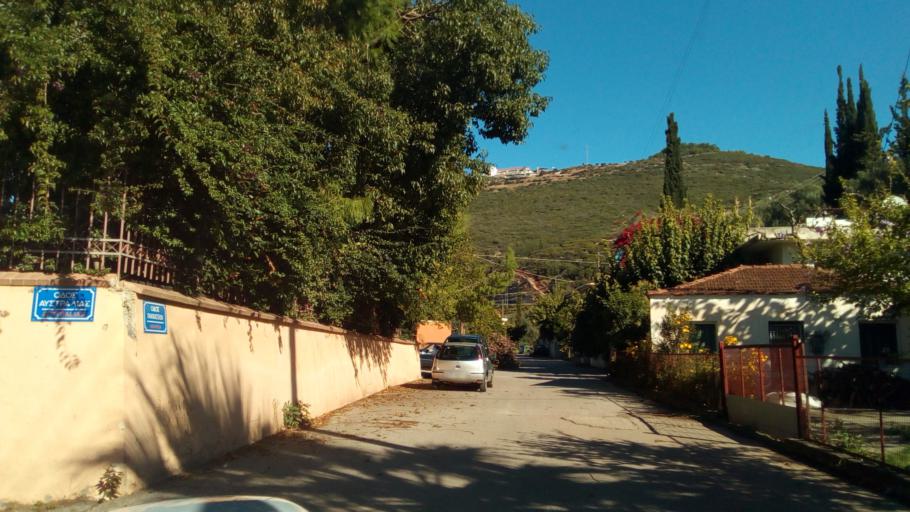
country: GR
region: West Greece
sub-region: Nomos Aitolias kai Akarnanias
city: Nafpaktos
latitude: 38.4072
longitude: 21.8546
